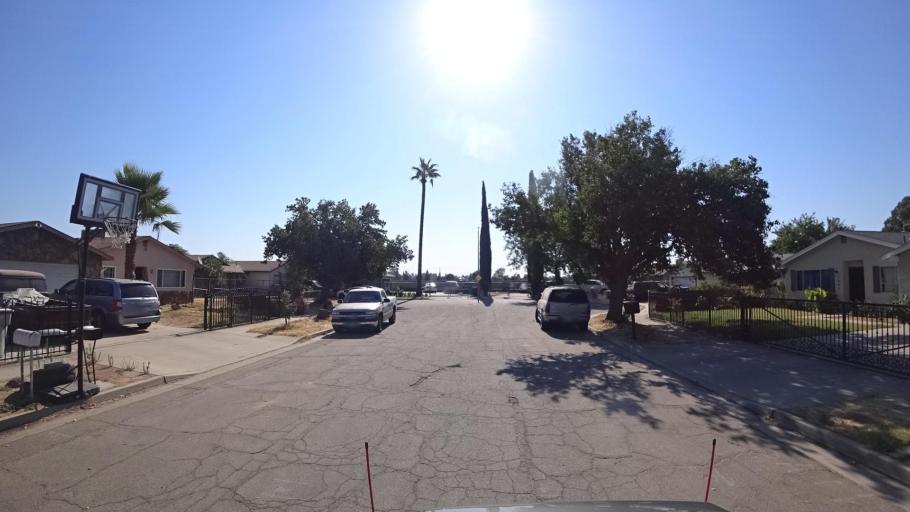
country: US
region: California
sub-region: Fresno County
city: West Park
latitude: 36.7265
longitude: -119.8300
